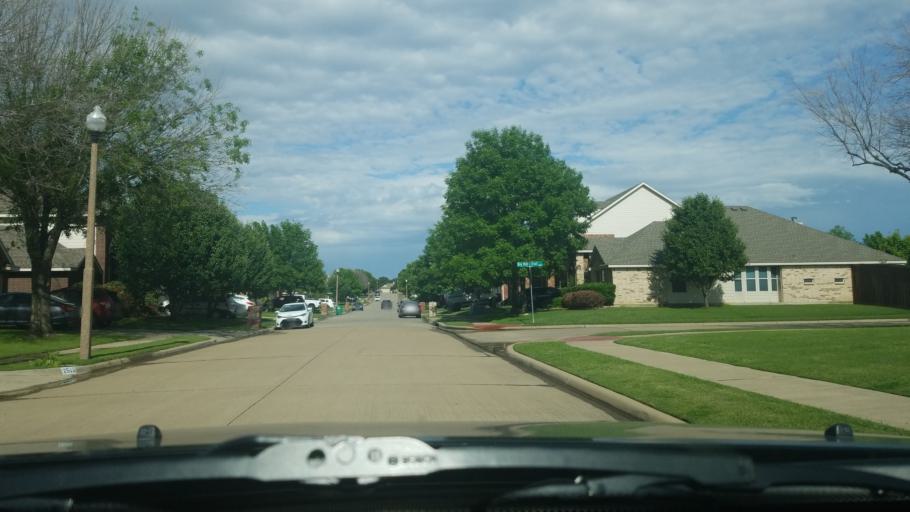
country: US
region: Texas
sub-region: Denton County
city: Corinth
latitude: 33.1707
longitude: -97.1064
